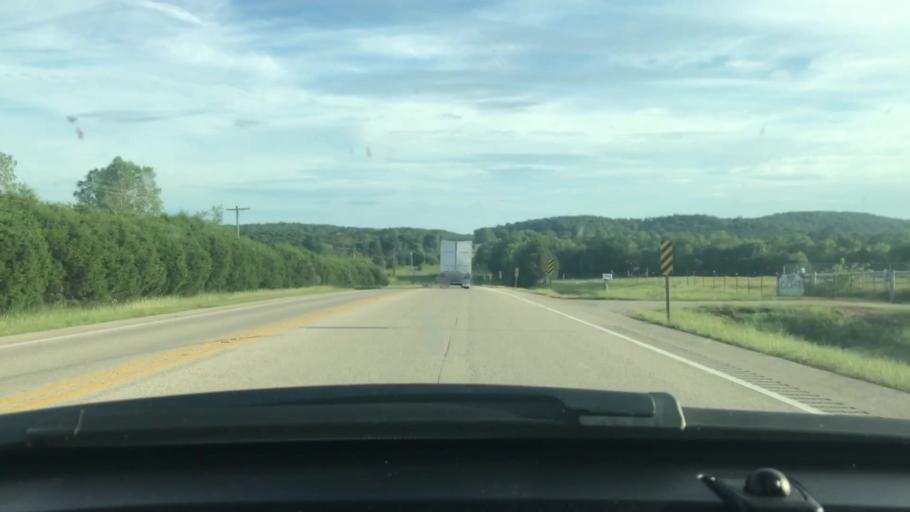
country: US
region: Arkansas
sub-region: Randolph County
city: Pocahontas
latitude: 36.1839
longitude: -91.1626
